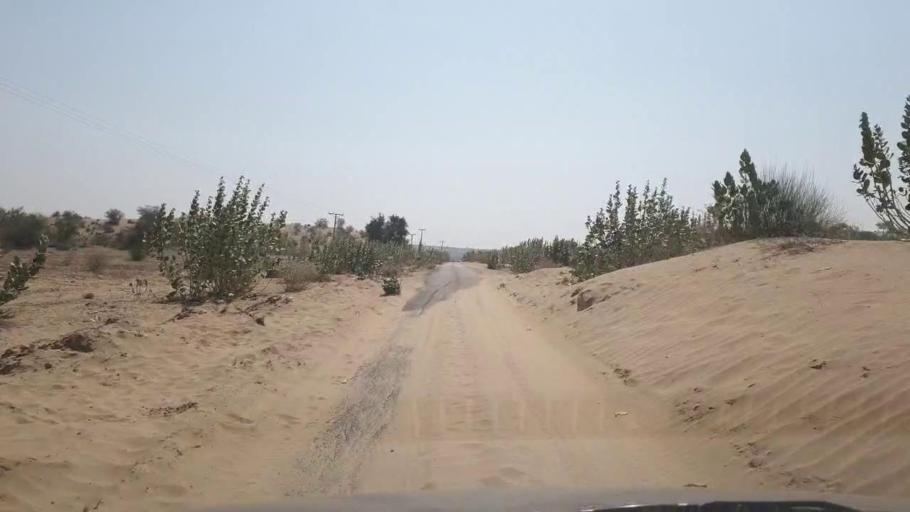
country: PK
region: Sindh
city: Chor
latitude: 25.6470
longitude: 70.1695
